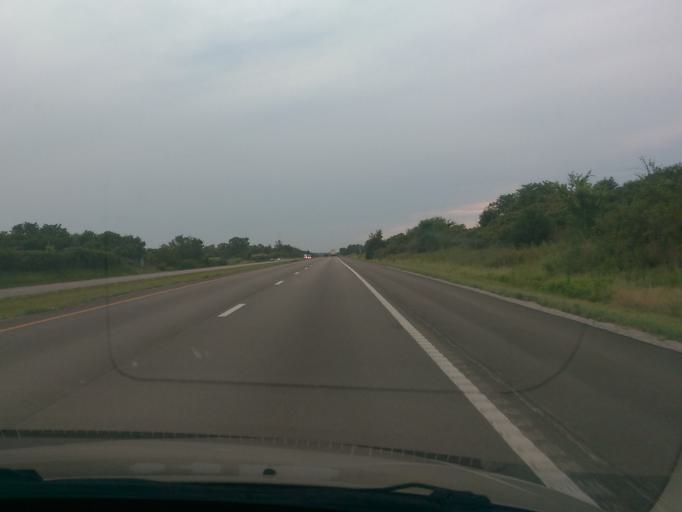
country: US
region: Missouri
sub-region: Andrew County
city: Savannah
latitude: 39.9485
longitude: -94.9469
